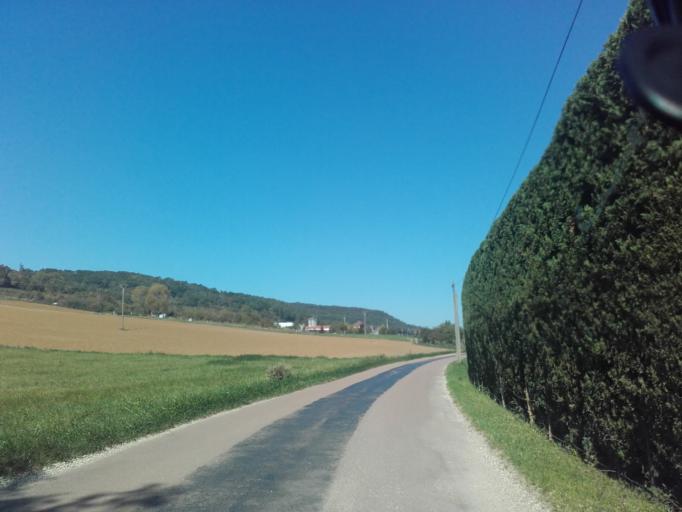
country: FR
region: Bourgogne
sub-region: Departement de la Cote-d'Or
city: Meursault
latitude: 47.0038
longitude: 4.7130
